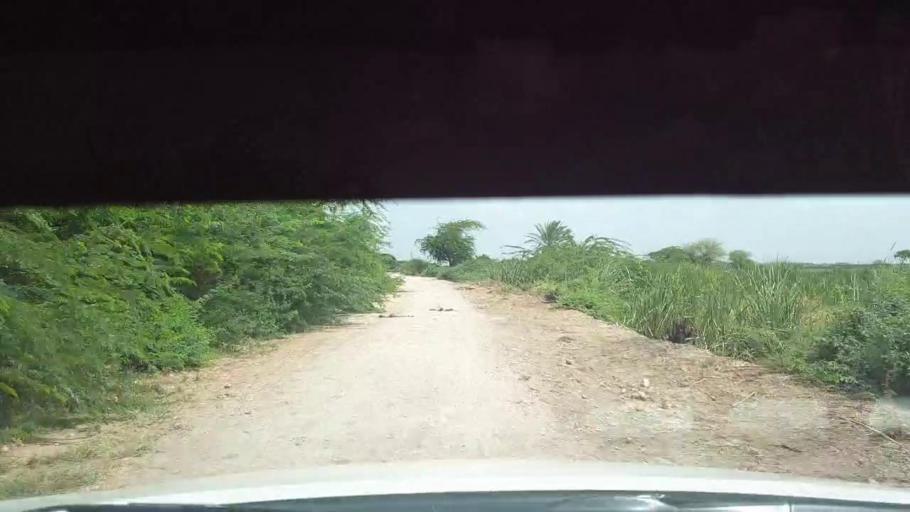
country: PK
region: Sindh
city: Kadhan
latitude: 24.4975
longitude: 68.9820
